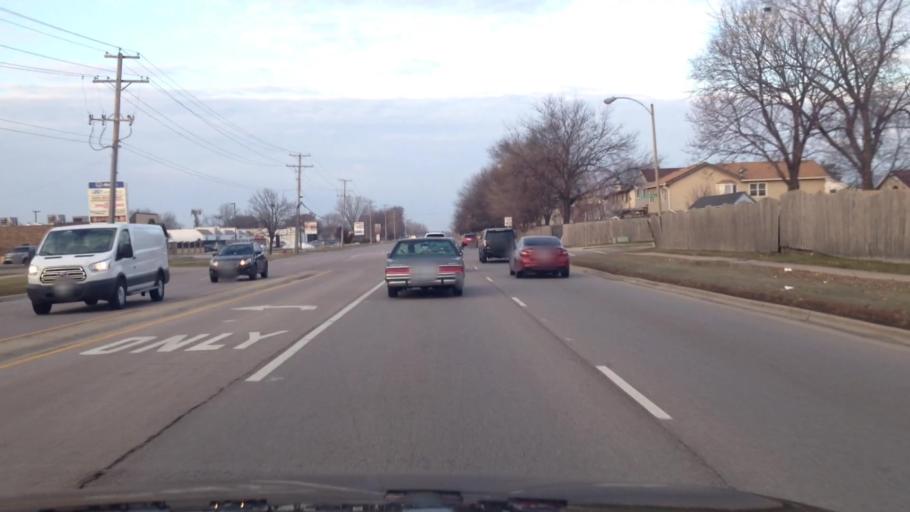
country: US
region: Illinois
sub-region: DuPage County
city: Hanover Park
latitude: 42.0325
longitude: -88.1445
